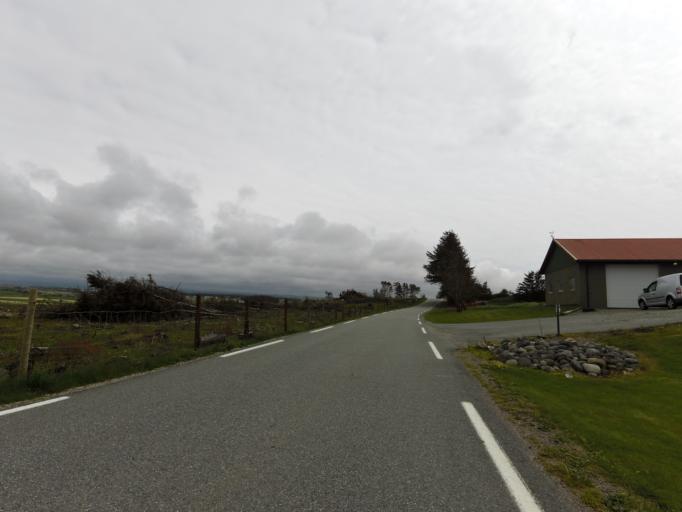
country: NO
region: Rogaland
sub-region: Ha
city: Naerbo
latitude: 58.6598
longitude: 5.5607
